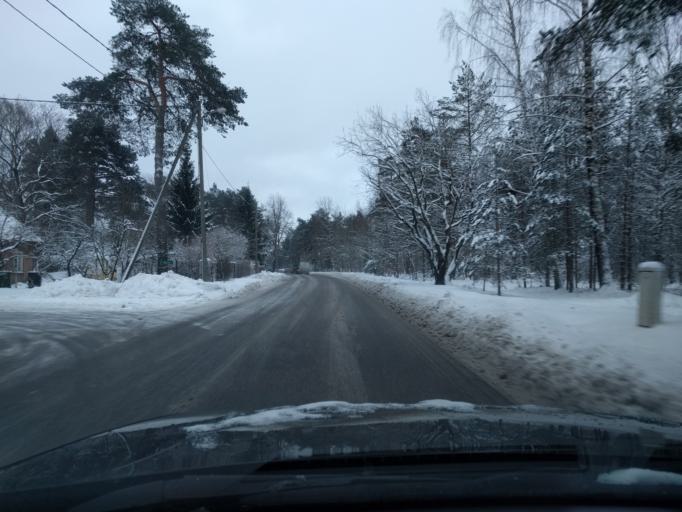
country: EE
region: Harju
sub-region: Saue vald
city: Laagri
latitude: 59.3782
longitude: 24.6698
